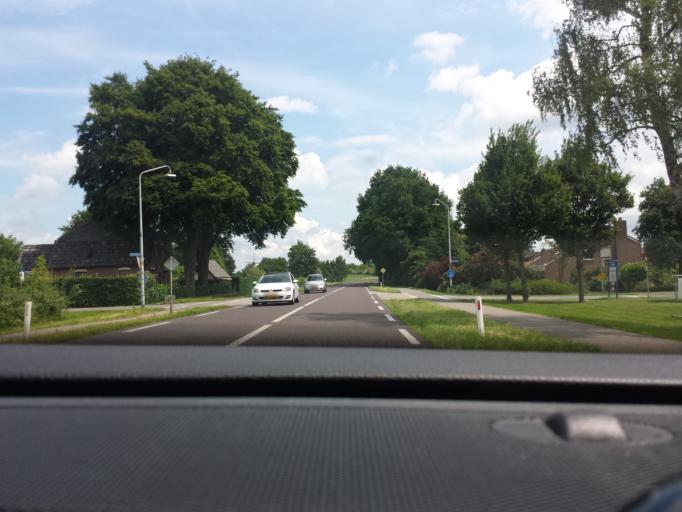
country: NL
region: Gelderland
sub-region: Berkelland
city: Neede
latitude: 52.1383
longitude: 6.5998
